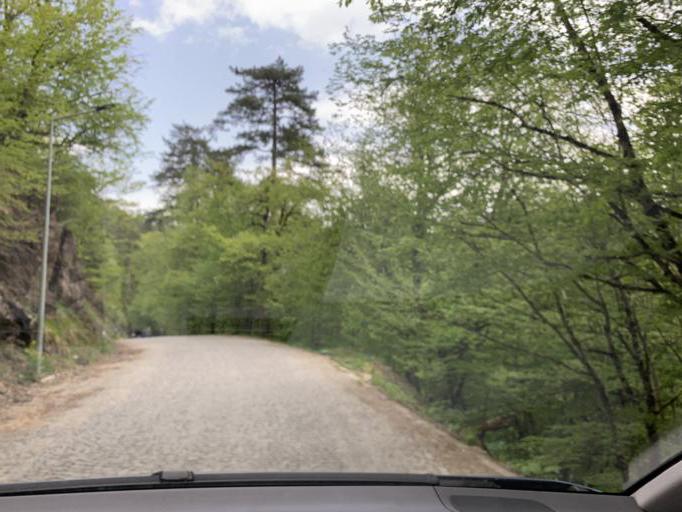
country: TR
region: Zonguldak
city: Egerci
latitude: 40.9373
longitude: 31.7409
